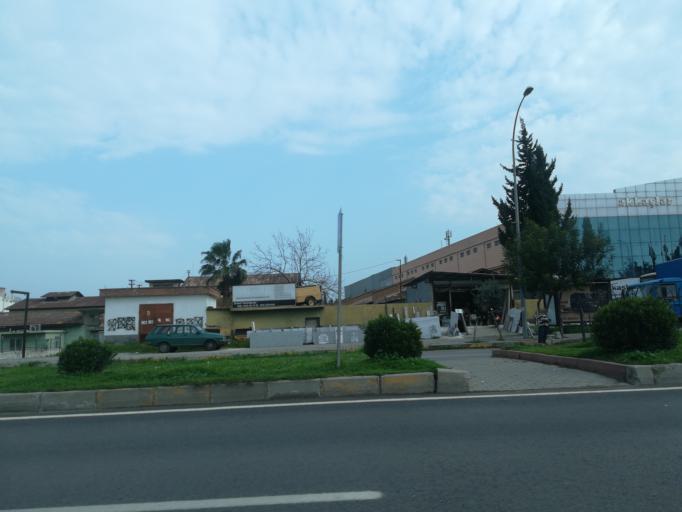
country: TR
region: Adana
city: Yuregir
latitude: 36.9870
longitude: 35.3540
